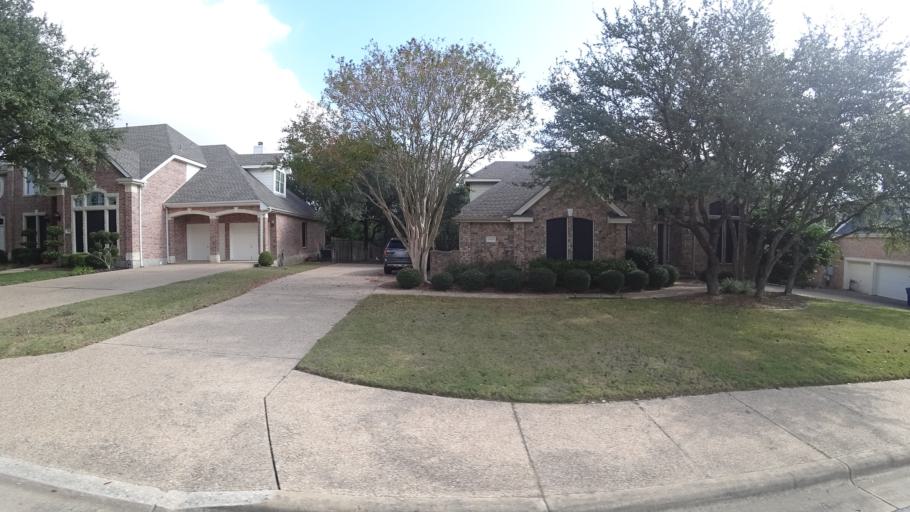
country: US
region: Texas
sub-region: Travis County
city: Barton Creek
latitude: 30.3113
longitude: -97.9016
